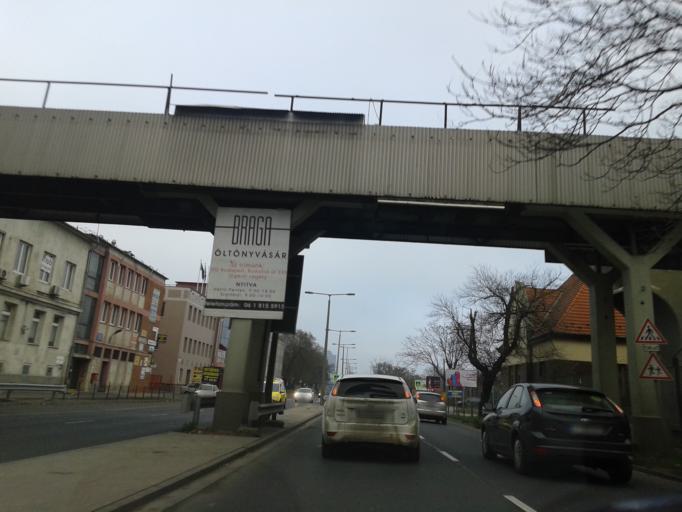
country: HU
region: Budapest
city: Budapest XI. keruelet
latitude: 47.4627
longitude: 19.0528
